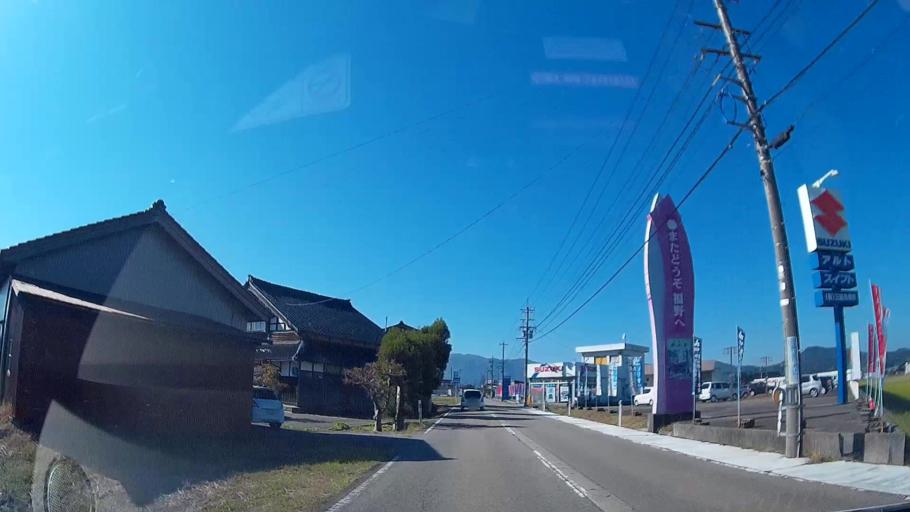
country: JP
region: Toyama
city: Nanto-shi
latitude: 36.5745
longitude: 136.8941
